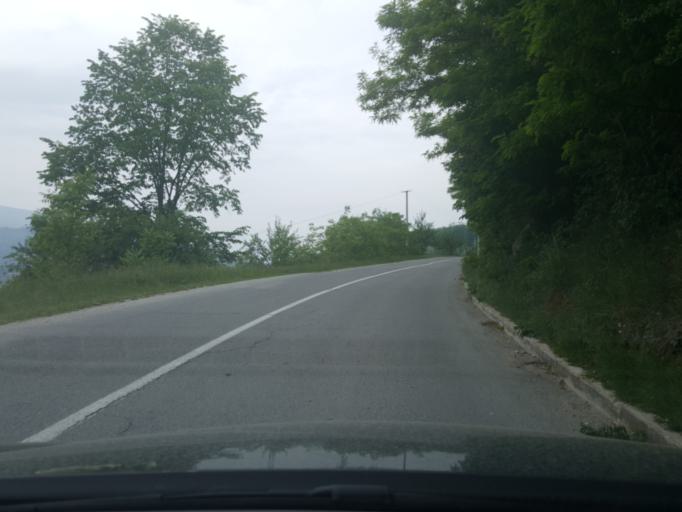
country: RS
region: Central Serbia
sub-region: Zlatiborski Okrug
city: Bajina Basta
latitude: 43.9421
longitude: 19.5684
